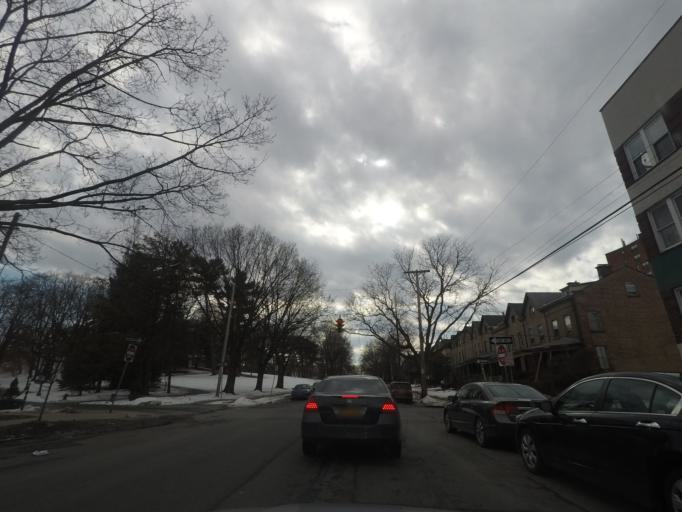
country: US
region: New York
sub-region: Albany County
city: Albany
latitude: 42.6596
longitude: -73.7758
